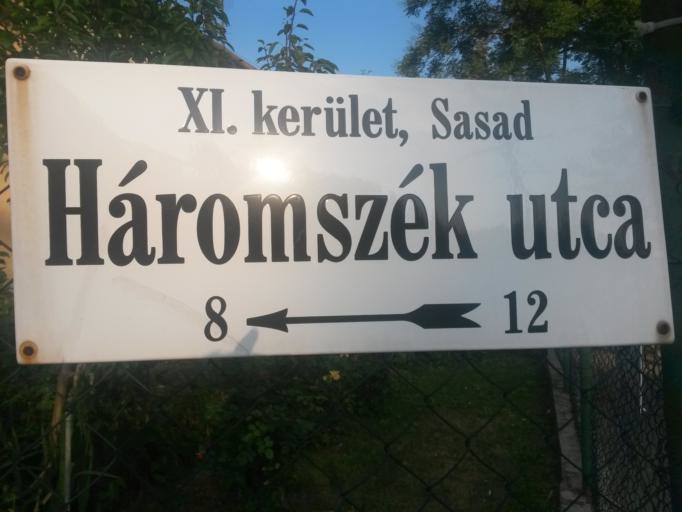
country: HU
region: Budapest
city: Budapest XII. keruelet
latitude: 47.4735
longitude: 19.0095
